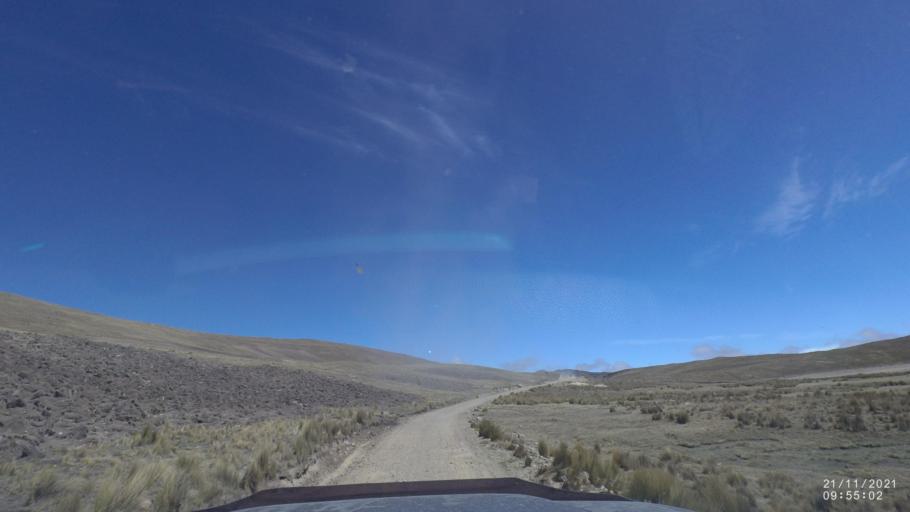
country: BO
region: Cochabamba
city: Cochabamba
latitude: -17.0502
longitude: -66.2629
